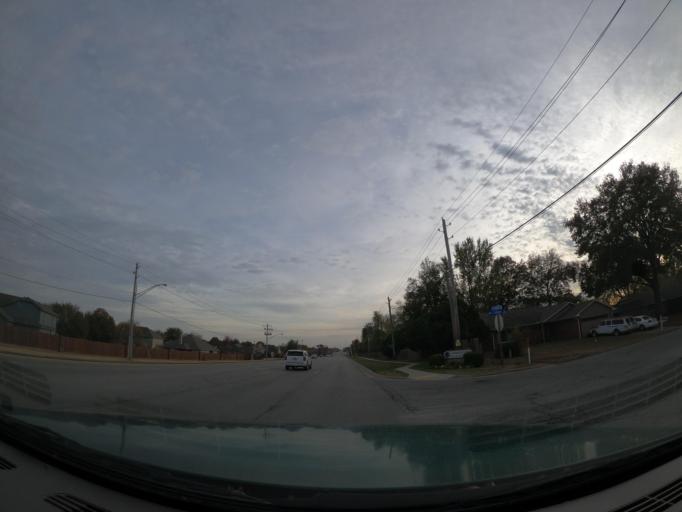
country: US
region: Oklahoma
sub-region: Tulsa County
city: Broken Arrow
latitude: 36.0533
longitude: -95.8154
